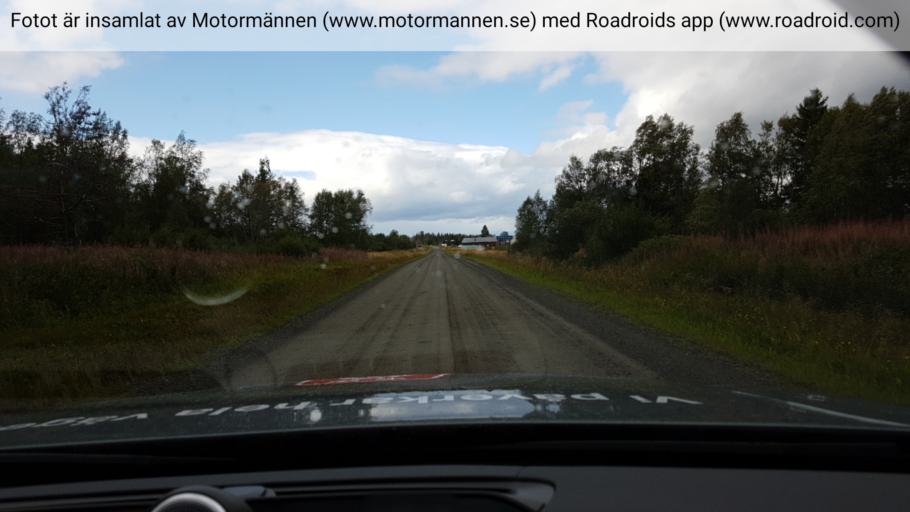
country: SE
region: Jaemtland
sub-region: OEstersunds Kommun
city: Lit
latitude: 63.6792
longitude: 14.8630
